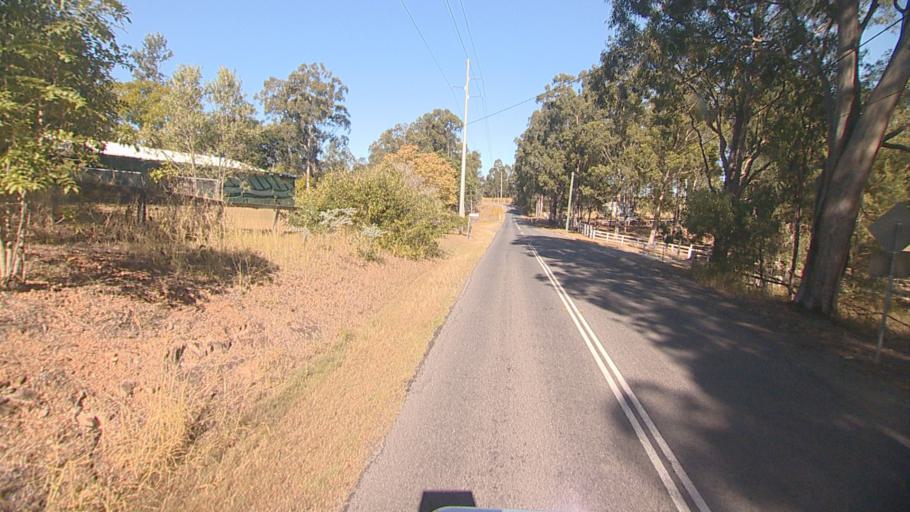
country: AU
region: Queensland
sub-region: Logan
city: Cedar Vale
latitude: -27.8865
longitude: 153.0174
